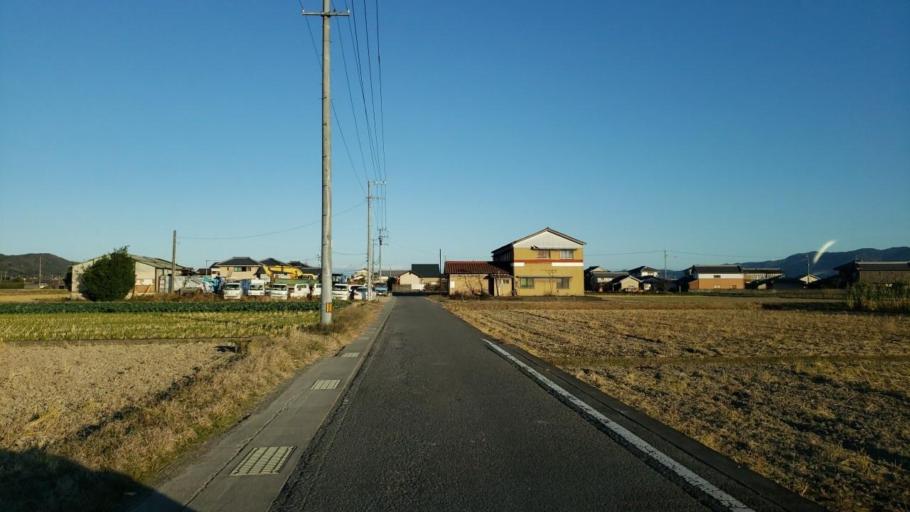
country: JP
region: Tokushima
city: Kamojimacho-jogejima
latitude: 34.0910
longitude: 134.2625
